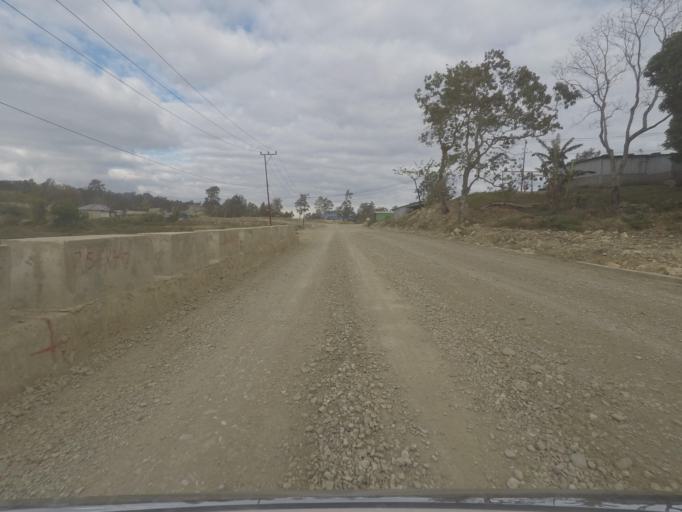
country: TL
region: Baucau
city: Venilale
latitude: -8.6345
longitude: 126.3785
